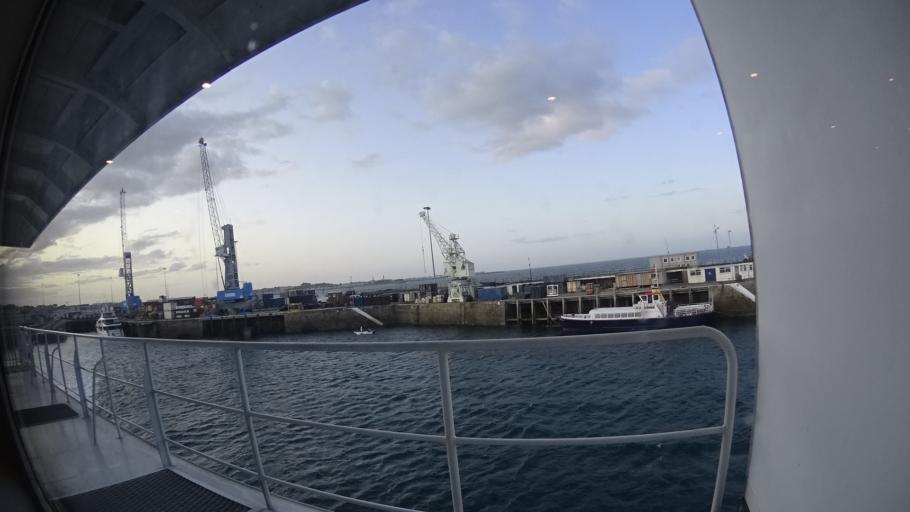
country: GG
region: St Peter Port
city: Saint Peter Port
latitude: 49.4565
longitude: -2.5275
